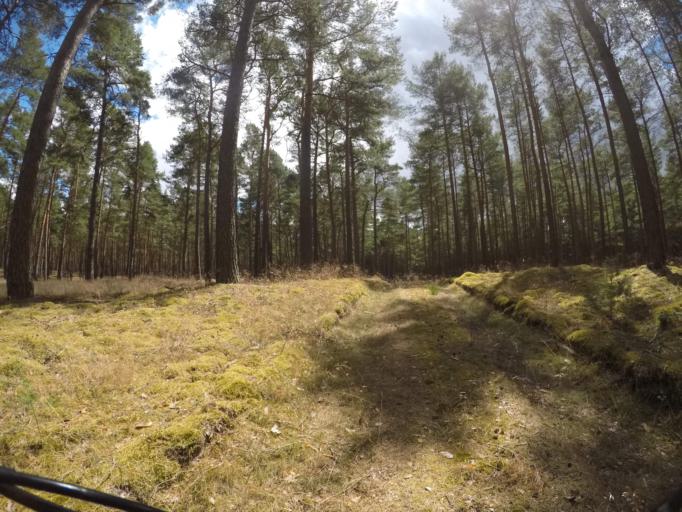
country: DE
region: Lower Saxony
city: Hitzacker
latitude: 53.1925
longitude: 11.0732
